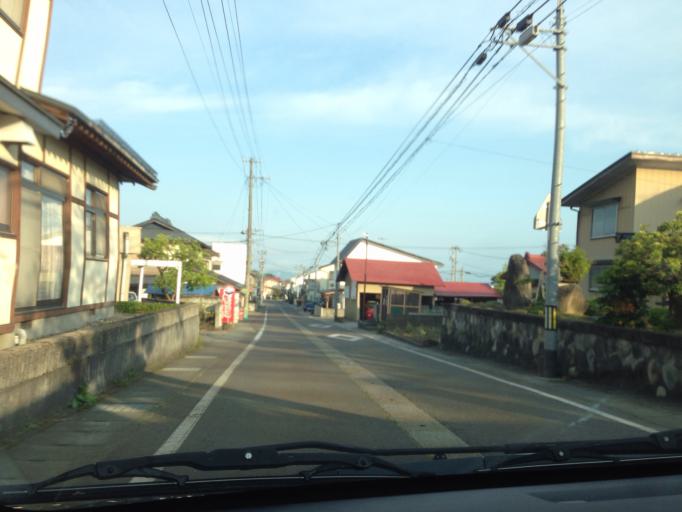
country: JP
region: Fukushima
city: Kitakata
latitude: 37.5517
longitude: 139.9306
